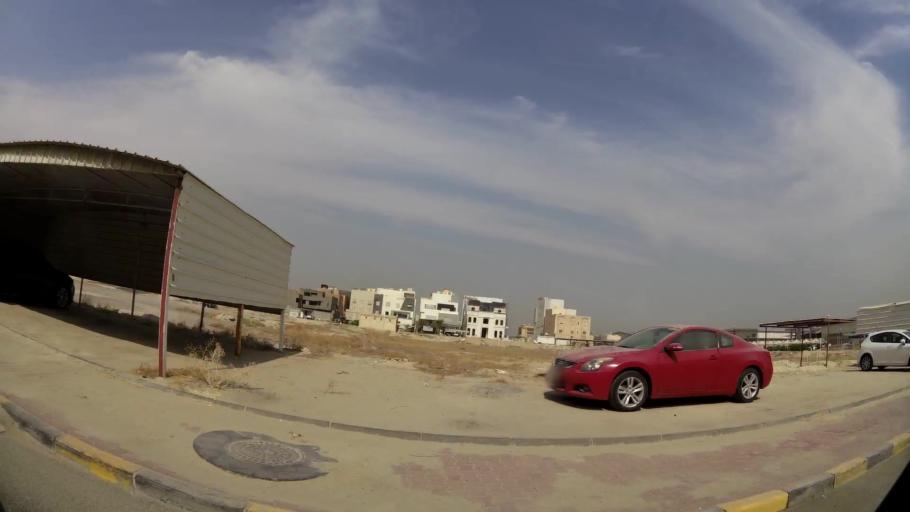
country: KW
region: Al Farwaniyah
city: Janub as Surrah
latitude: 29.2893
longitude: 47.9898
